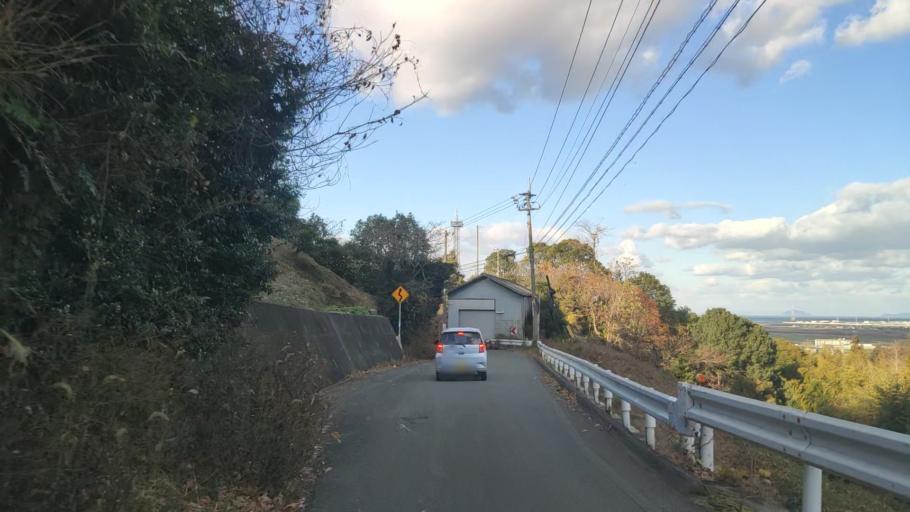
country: JP
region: Ehime
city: Saijo
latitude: 33.8848
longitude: 133.1306
